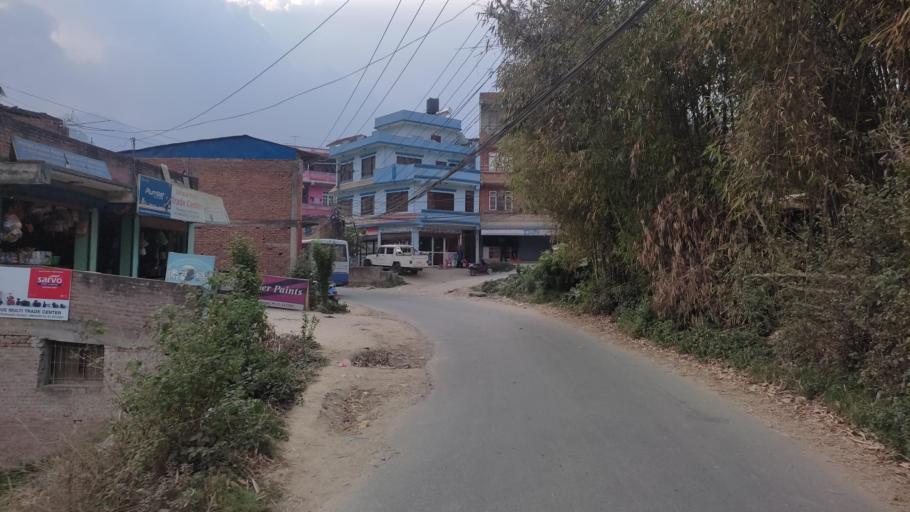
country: NP
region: Central Region
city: Kirtipur
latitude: 27.6665
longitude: 85.2630
